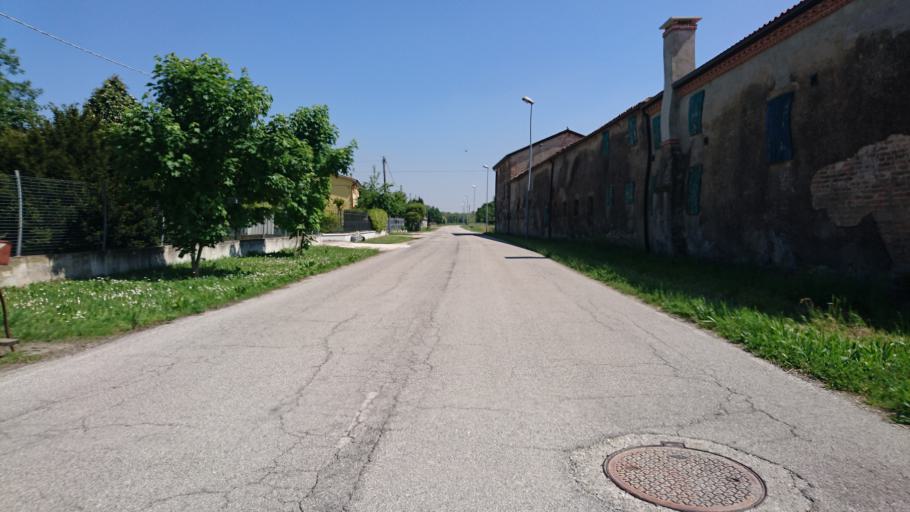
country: IT
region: Veneto
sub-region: Provincia di Padova
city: Casalserugo
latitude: 45.2980
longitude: 11.9128
